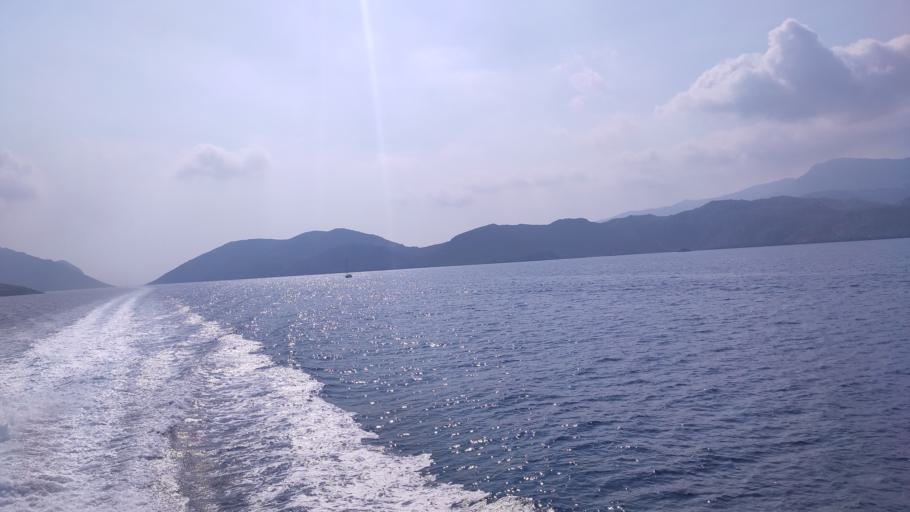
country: GR
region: South Aegean
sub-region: Nomos Dodekanisou
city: Symi
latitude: 36.6443
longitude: 27.7950
